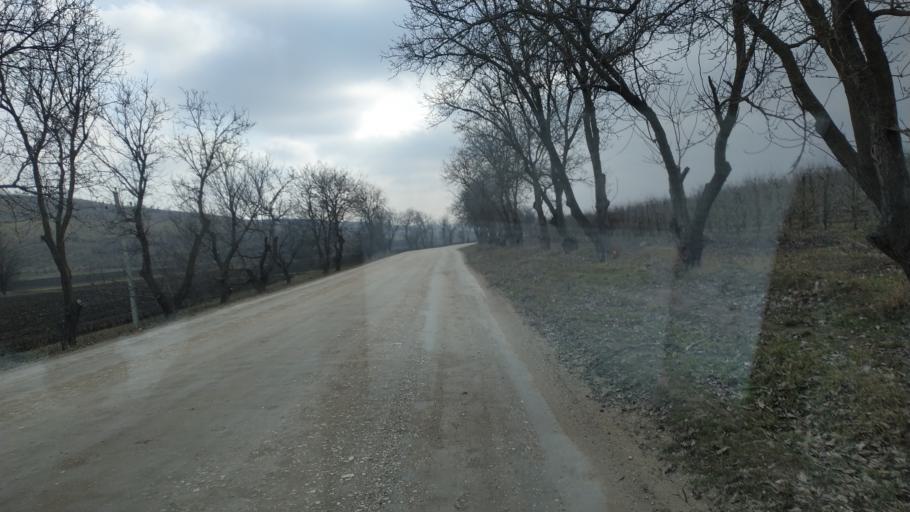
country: MD
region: Hincesti
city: Dancu
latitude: 46.9130
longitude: 28.3292
